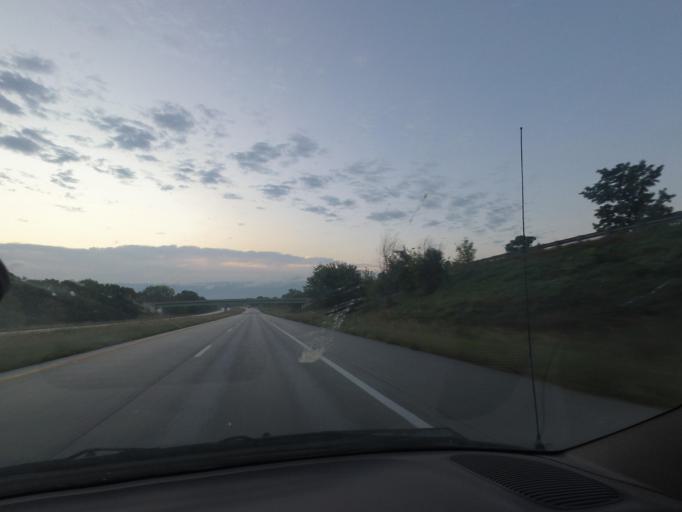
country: US
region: Missouri
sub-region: Macon County
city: Macon
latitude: 39.7521
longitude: -92.5322
